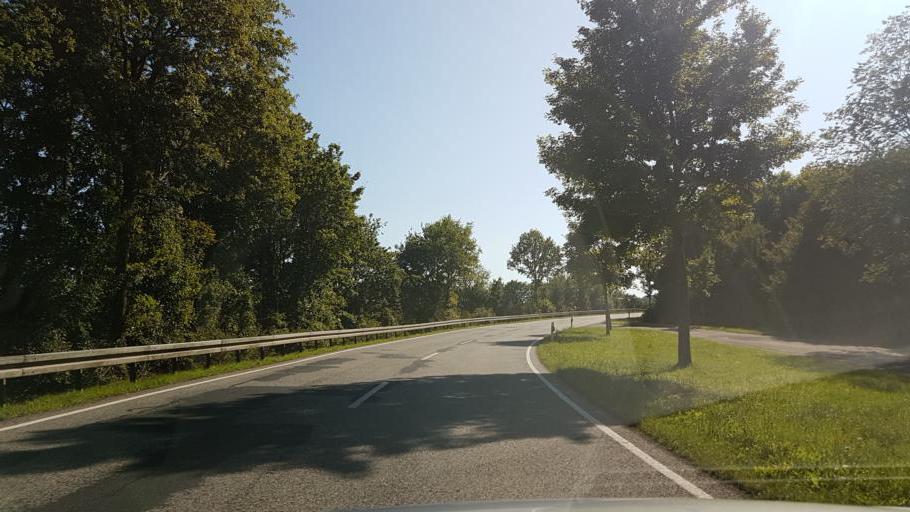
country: DE
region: Saarland
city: Tholey
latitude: 49.4969
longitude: 6.9927
